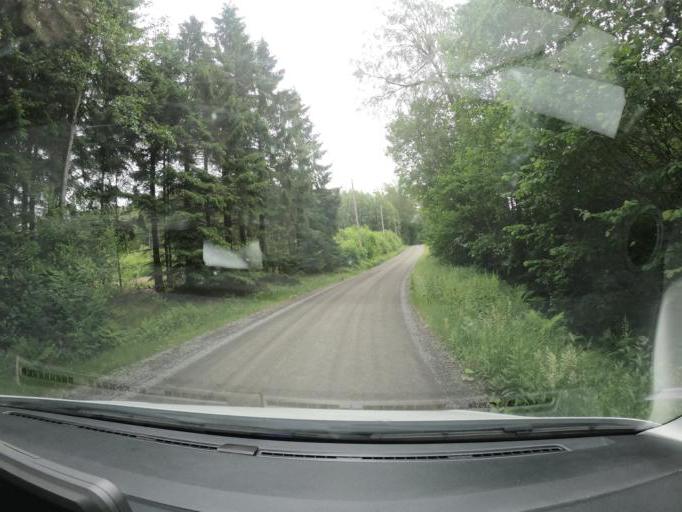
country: SE
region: Skane
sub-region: Hoors Kommun
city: Hoeoer
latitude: 55.9808
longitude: 13.5061
